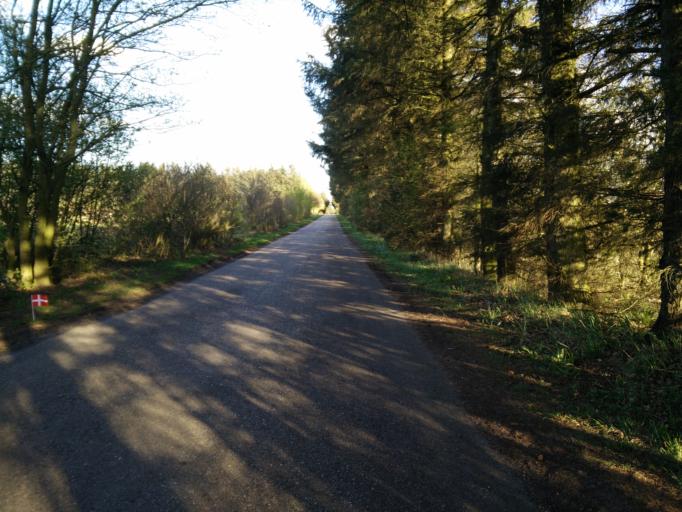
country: DK
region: Central Jutland
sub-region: Ringkobing-Skjern Kommune
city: Tarm
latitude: 55.8339
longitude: 8.4652
